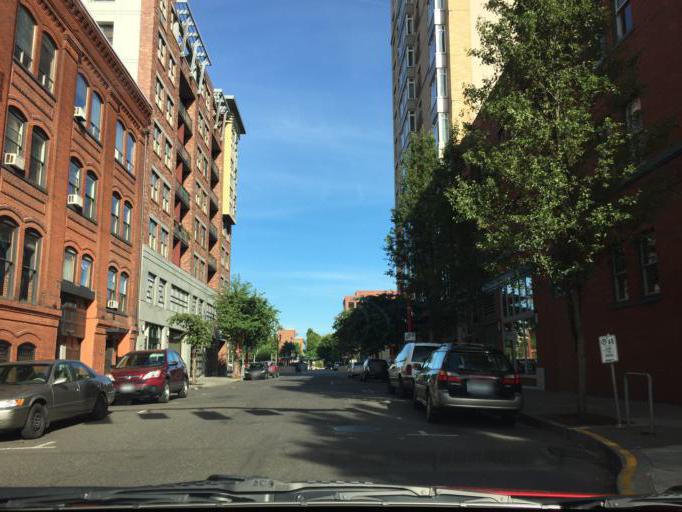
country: US
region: Oregon
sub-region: Multnomah County
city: Portland
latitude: 45.5259
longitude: -122.6755
